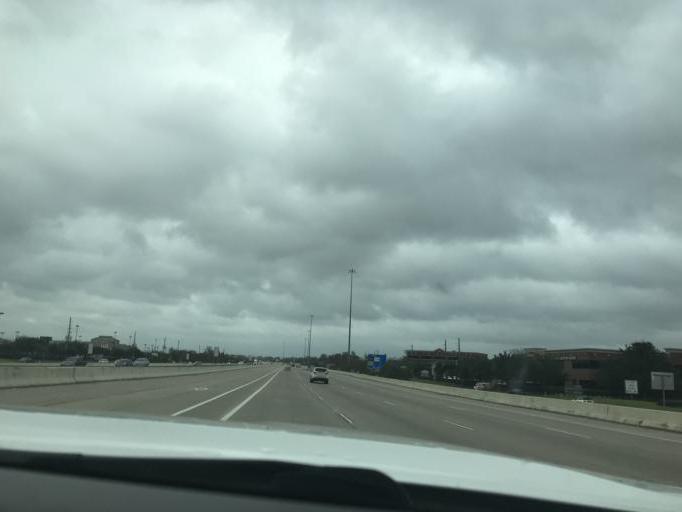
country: US
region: Texas
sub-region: Fort Bend County
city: Greatwood
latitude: 29.5623
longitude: -95.6856
